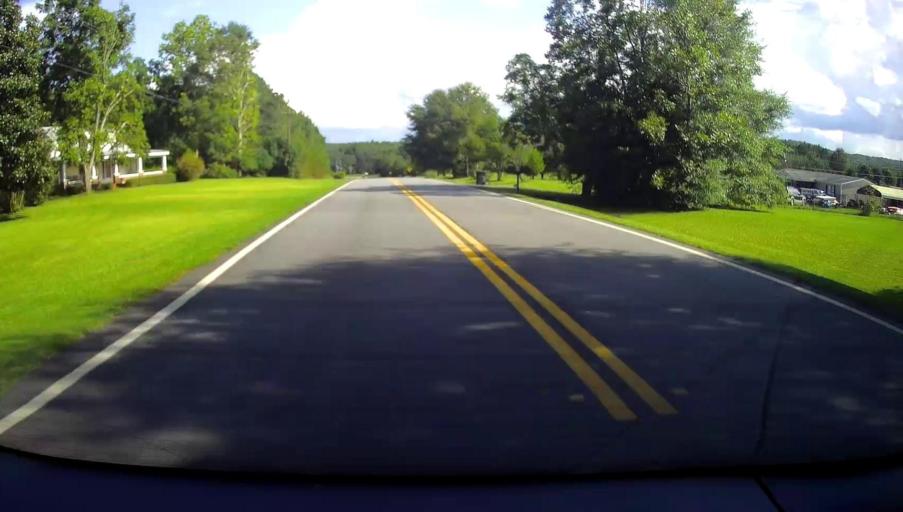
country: US
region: Georgia
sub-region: Upson County
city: Hannahs Mill
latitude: 32.9244
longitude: -84.4404
